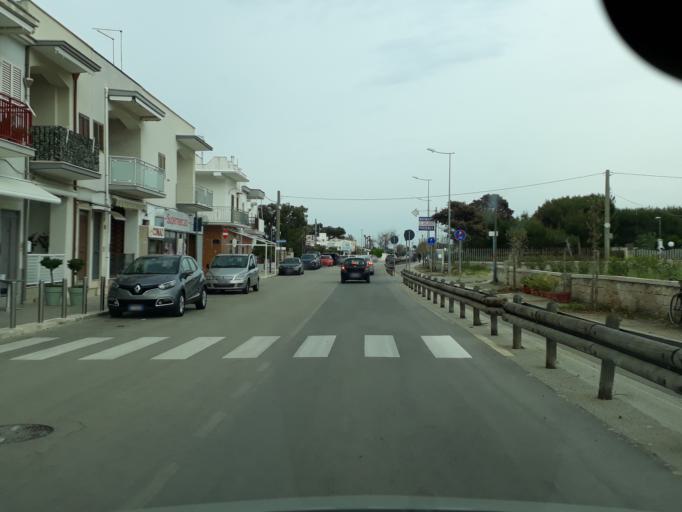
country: IT
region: Apulia
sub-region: Provincia di Brindisi
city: Ostuni
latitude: 40.7872
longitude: 17.5948
